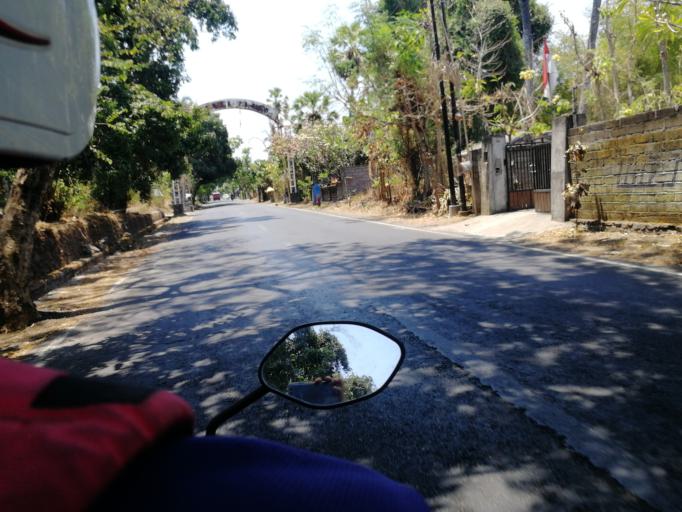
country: ID
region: Bali
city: Banjar Trunyan
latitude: -8.1437
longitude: 115.3960
